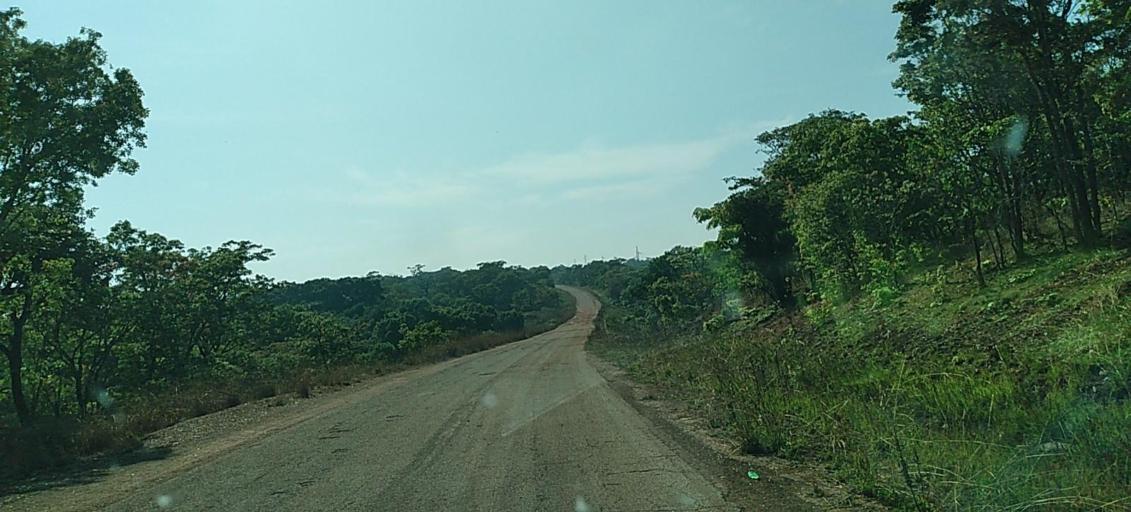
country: ZM
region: North-Western
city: Mwinilunga
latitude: -11.7852
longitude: 25.0446
